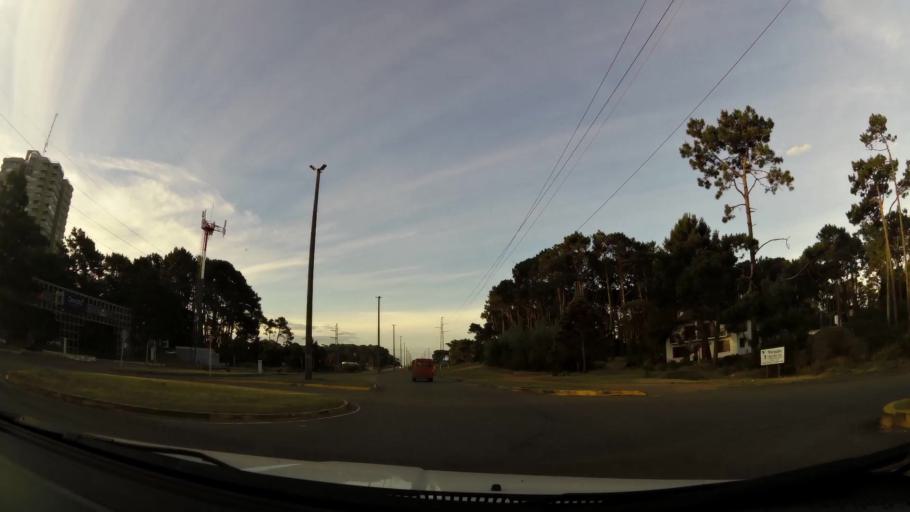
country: UY
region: Maldonado
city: Maldonado
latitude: -34.9324
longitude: -54.9391
